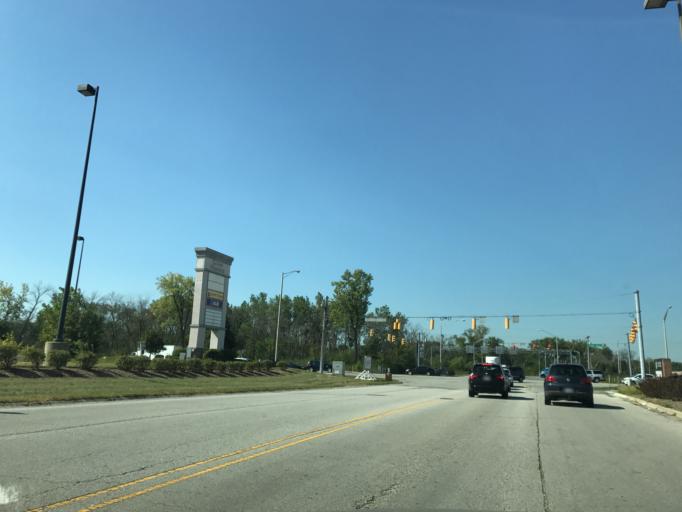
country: US
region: Indiana
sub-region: Lake County
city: Hammond
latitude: 41.5708
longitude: -87.4759
